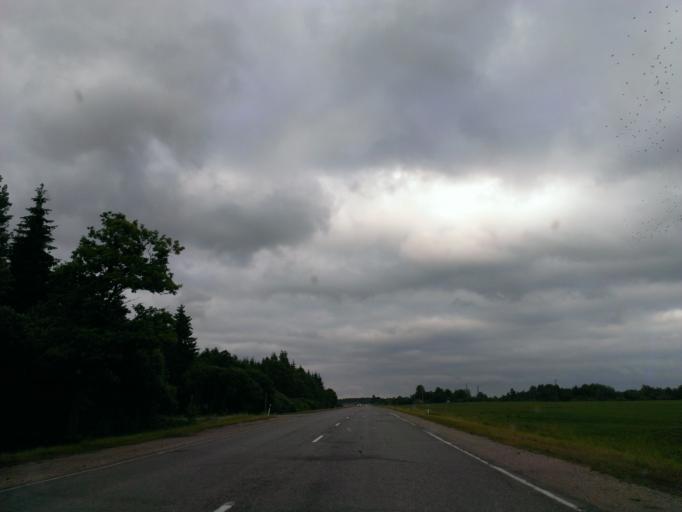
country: LV
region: Saldus Rajons
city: Saldus
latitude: 56.6700
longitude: 22.4014
